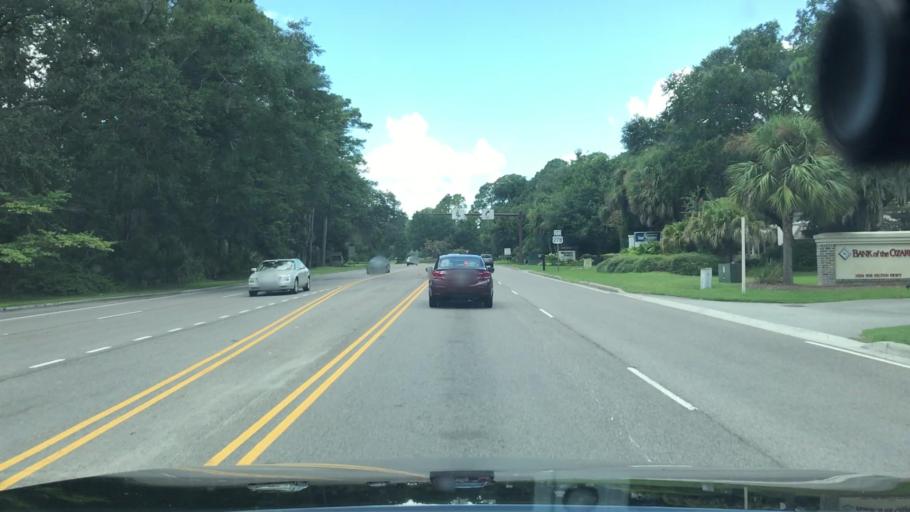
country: US
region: South Carolina
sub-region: Beaufort County
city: Hilton Head Island
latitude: 32.1564
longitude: -80.7603
